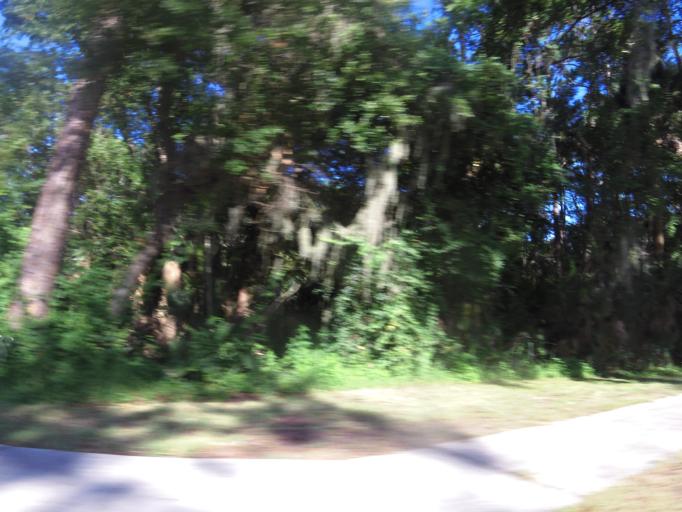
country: US
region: Florida
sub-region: Nassau County
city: Fernandina Beach
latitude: 30.6228
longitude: -81.4553
